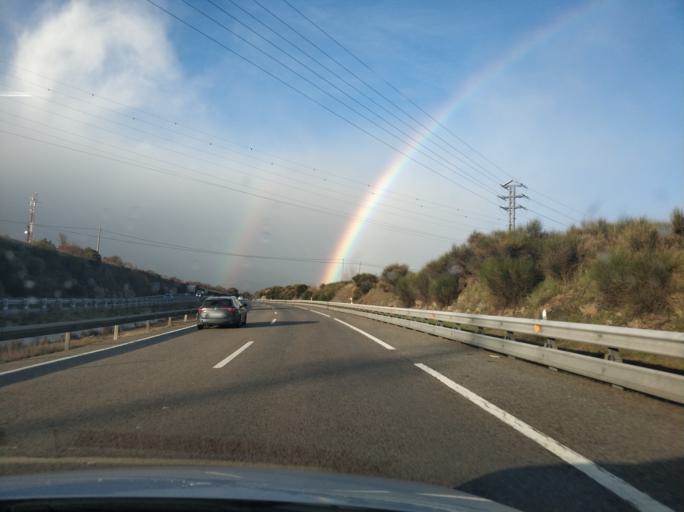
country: ES
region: Madrid
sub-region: Provincia de Madrid
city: Buitrago del Lozoya
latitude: 41.0029
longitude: -3.6373
